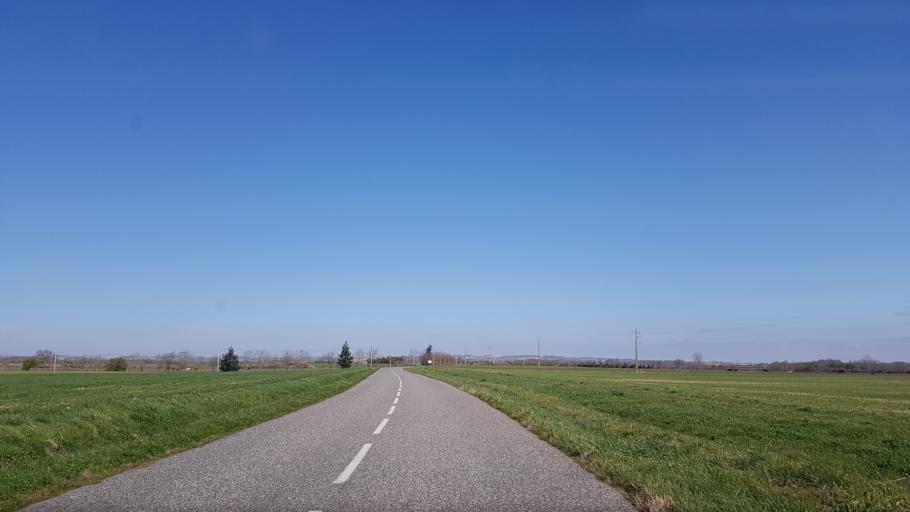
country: FR
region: Languedoc-Roussillon
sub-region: Departement de l'Aude
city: Belpech
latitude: 43.1543
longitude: 1.7067
